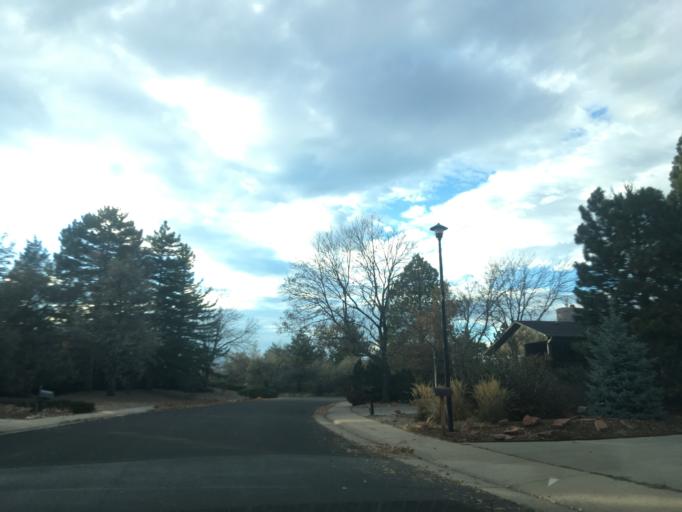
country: US
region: Colorado
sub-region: Boulder County
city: Louisville
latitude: 39.9885
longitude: -105.1623
